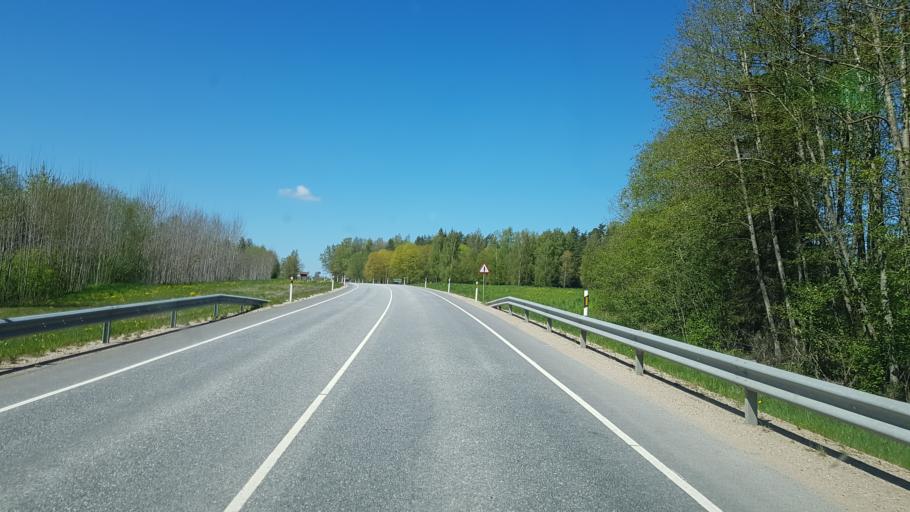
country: EE
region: Viljandimaa
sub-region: Viiratsi vald
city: Viiratsi
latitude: 58.3325
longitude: 25.6527
